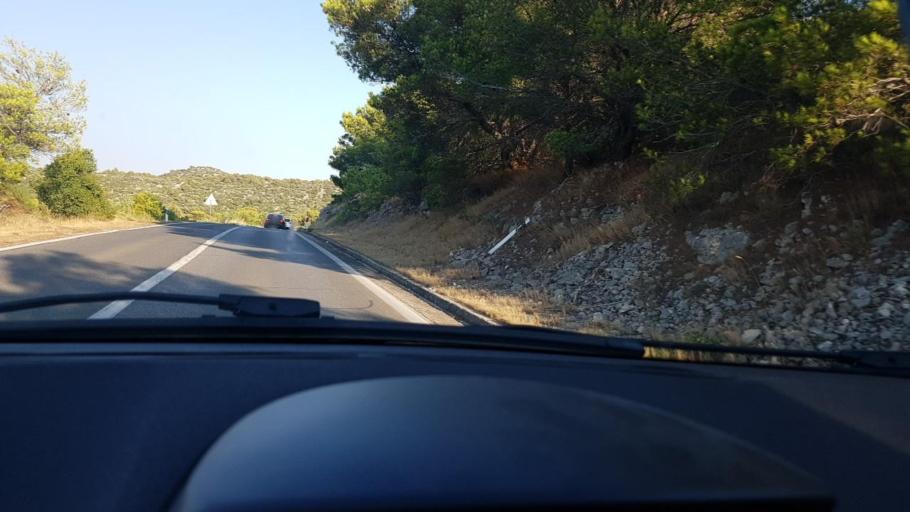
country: HR
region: Sibensko-Kniniska
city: Murter
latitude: 43.8071
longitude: 15.6062
